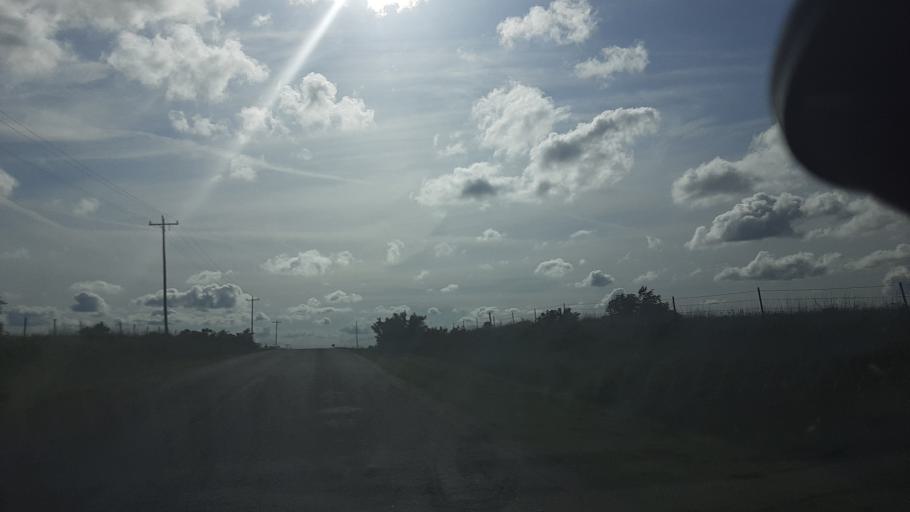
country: US
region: Oklahoma
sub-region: Logan County
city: Langston
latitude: 36.0579
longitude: -97.3794
